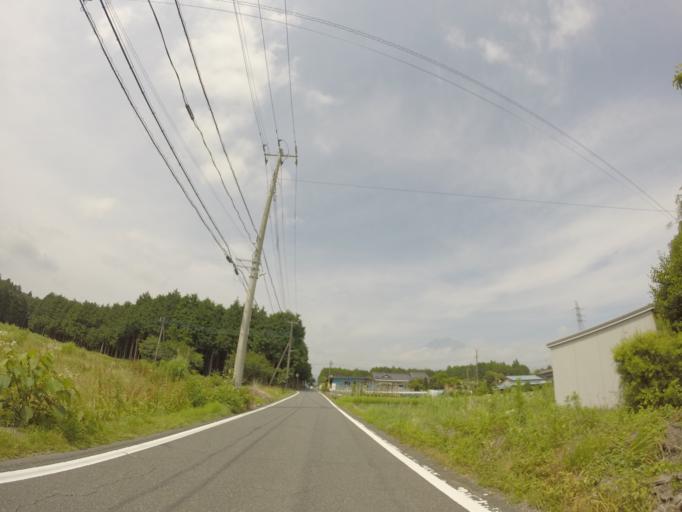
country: JP
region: Shizuoka
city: Fujinomiya
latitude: 35.2942
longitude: 138.5831
